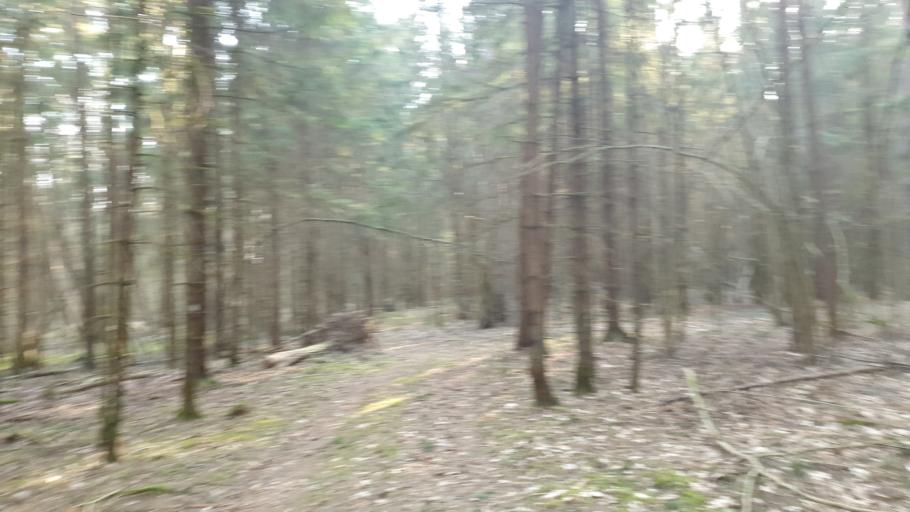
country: LT
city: Nemencine
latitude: 54.8746
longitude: 25.5720
